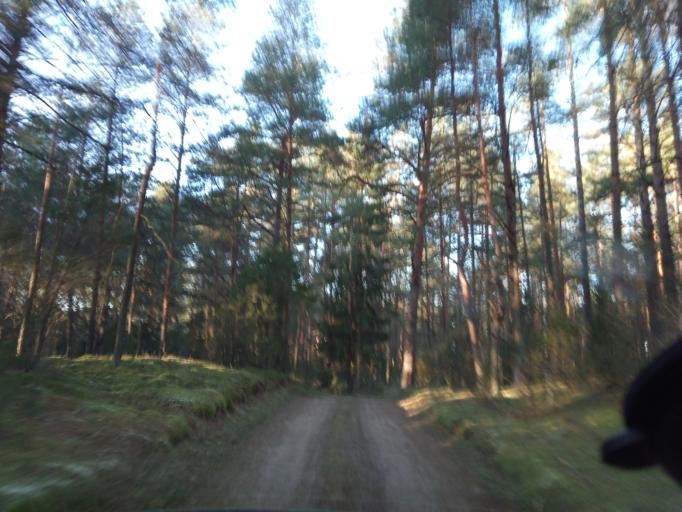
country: LT
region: Alytaus apskritis
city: Druskininkai
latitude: 53.9668
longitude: 23.9702
